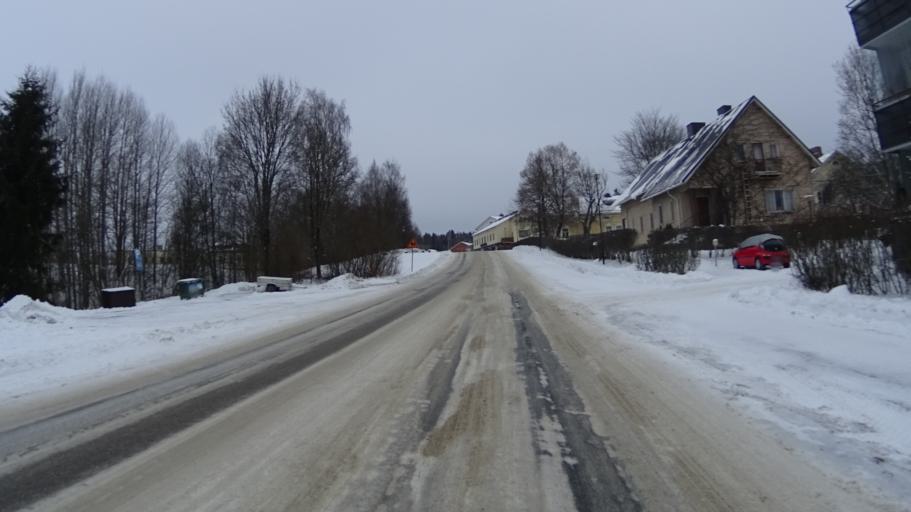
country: FI
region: Uusimaa
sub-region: Helsinki
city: Karkkila
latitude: 60.5336
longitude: 24.2064
